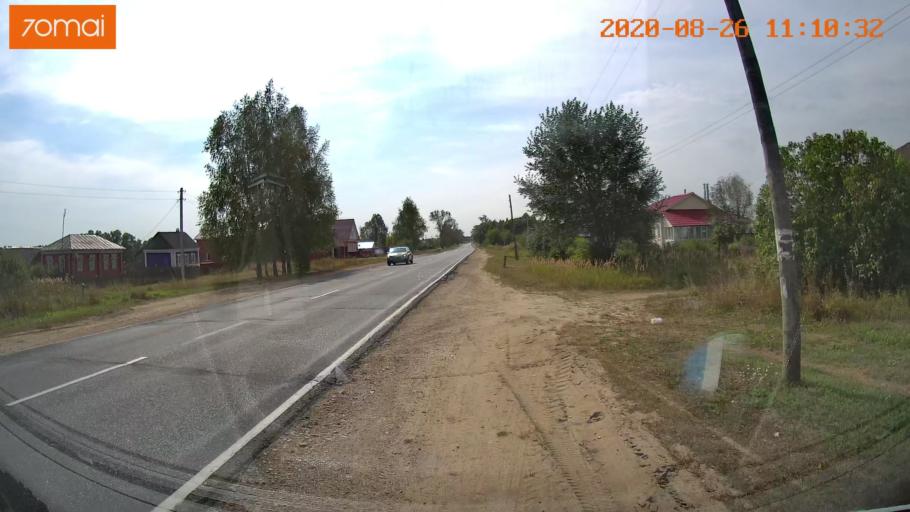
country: RU
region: Rjazan
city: Izhevskoye
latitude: 54.4776
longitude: 41.1261
